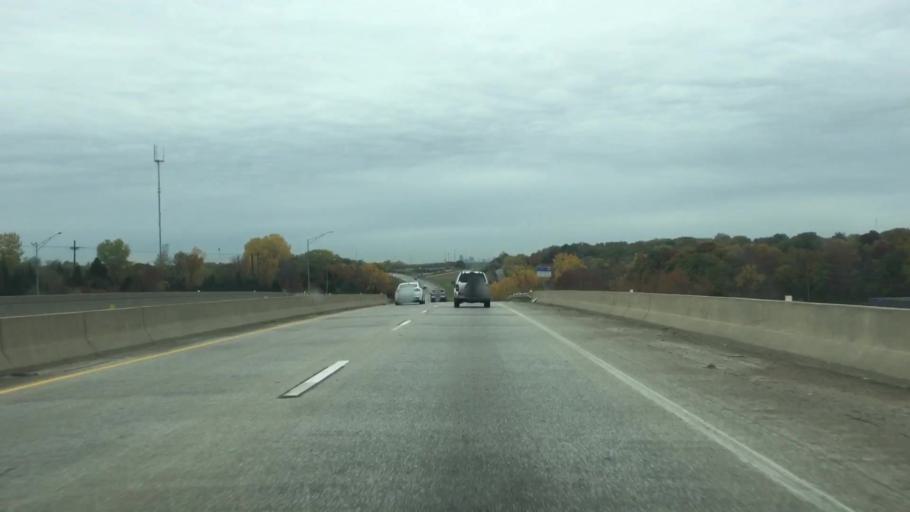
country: US
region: Missouri
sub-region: Jackson County
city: Raytown
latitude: 39.0096
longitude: -94.4889
